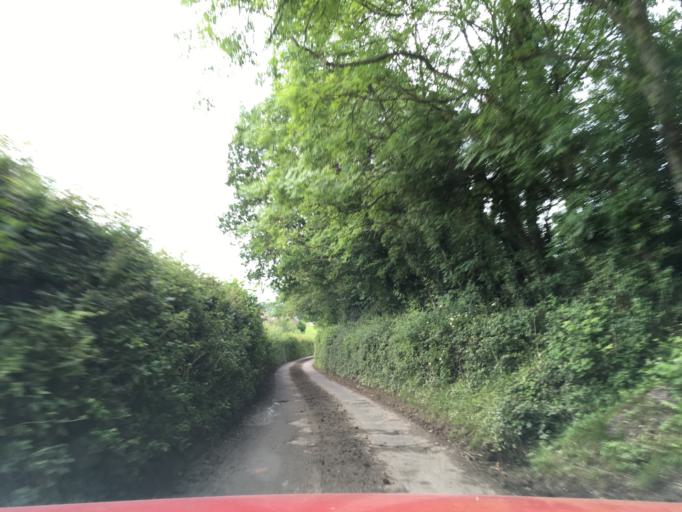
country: GB
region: England
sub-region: South Gloucestershire
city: Horton
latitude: 51.5836
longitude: -2.3456
